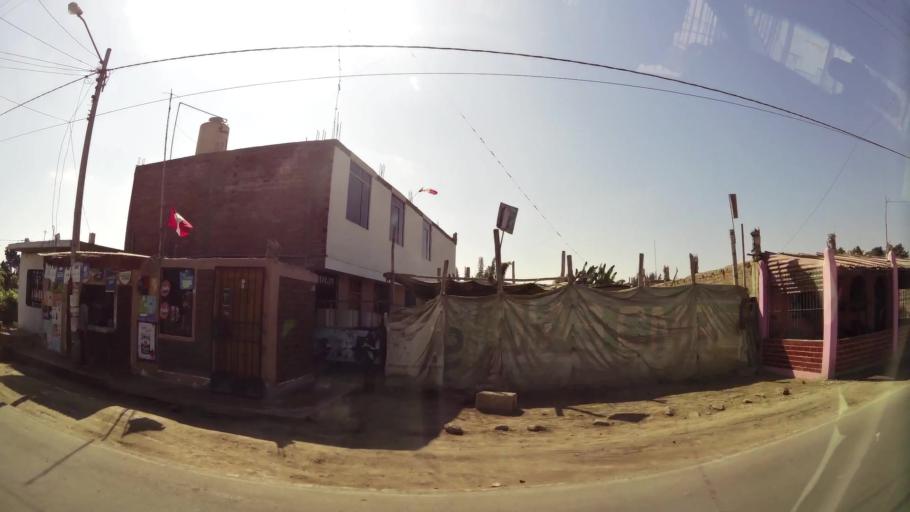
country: PE
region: Ica
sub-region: Provincia de Chincha
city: Sunampe
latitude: -13.4192
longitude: -76.1622
